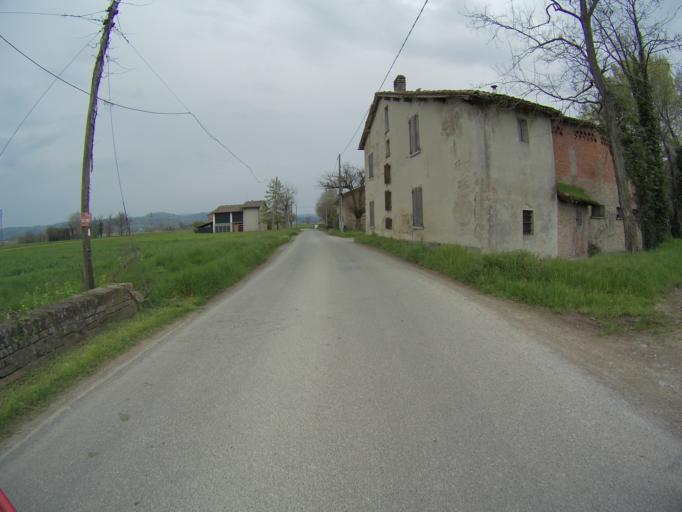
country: IT
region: Emilia-Romagna
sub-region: Provincia di Reggio Emilia
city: San Polo d'Enza
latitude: 44.6595
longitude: 10.4359
